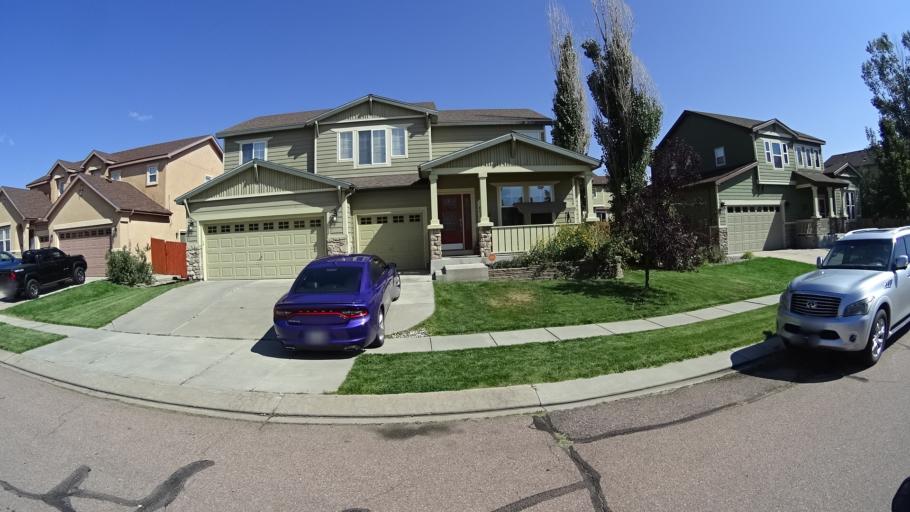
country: US
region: Colorado
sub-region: El Paso County
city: Cimarron Hills
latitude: 38.9207
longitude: -104.6979
